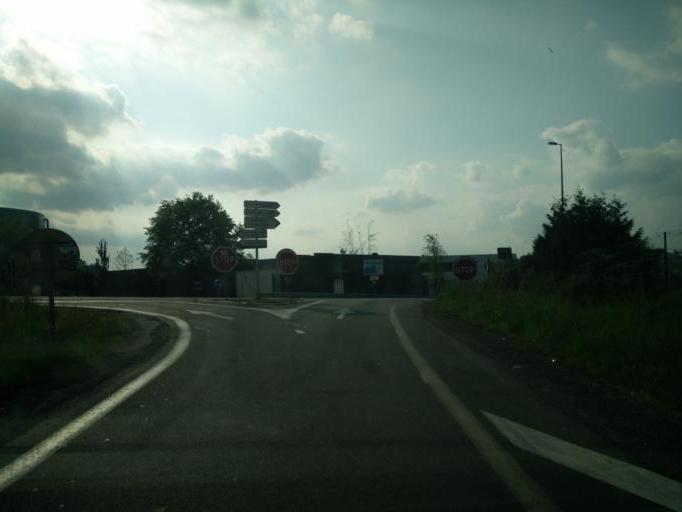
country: FR
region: Brittany
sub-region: Departement du Finistere
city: Quimperle
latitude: 47.8630
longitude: -3.5513
